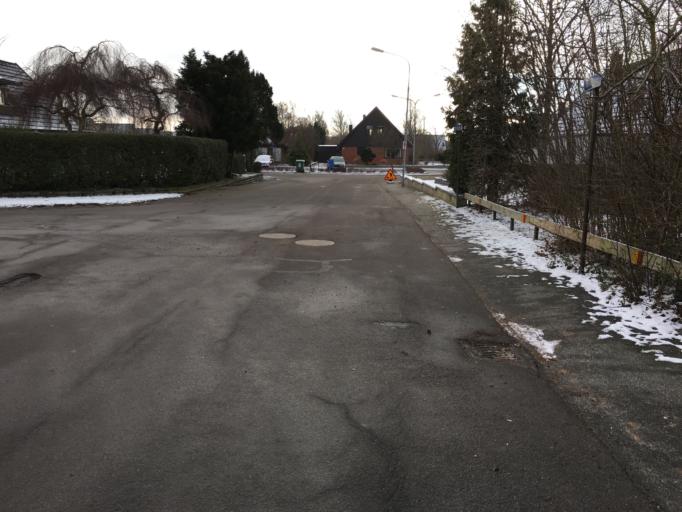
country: SE
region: Skane
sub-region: Vellinge Kommun
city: Vellinge
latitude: 55.4770
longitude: 13.0361
